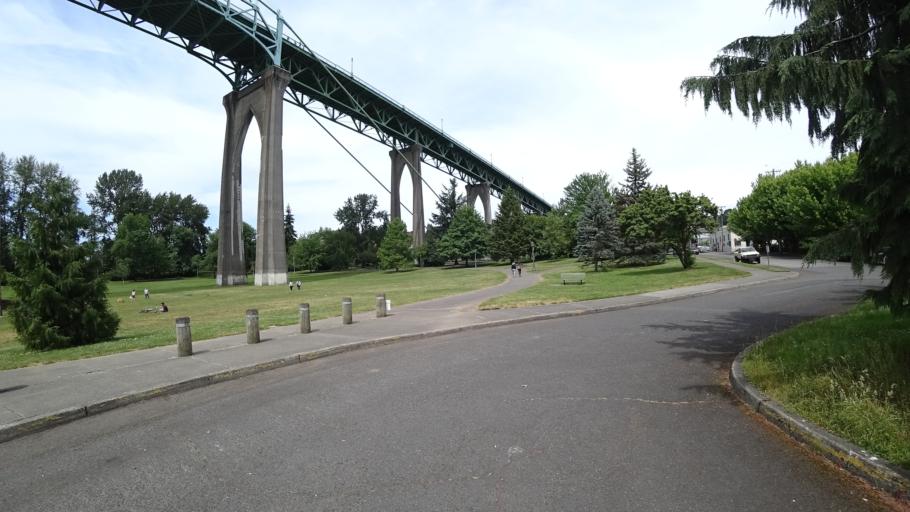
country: US
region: Oregon
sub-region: Washington County
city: West Haven
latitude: 45.5861
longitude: -122.7611
